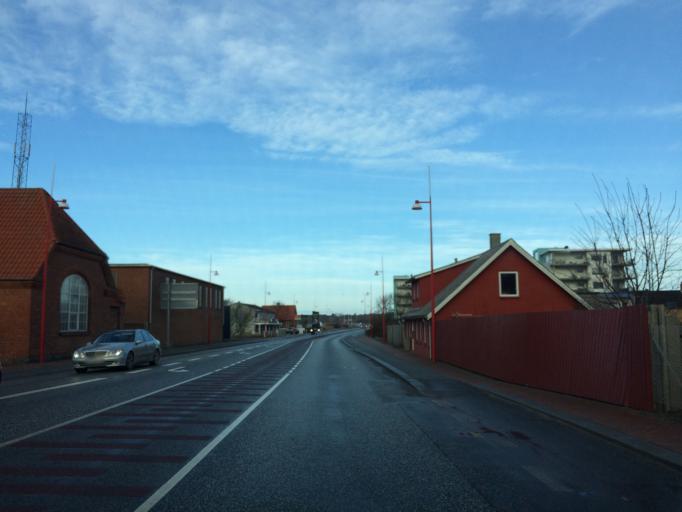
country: DK
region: Central Jutland
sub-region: Struer Kommune
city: Struer
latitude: 56.4933
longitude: 8.5837
